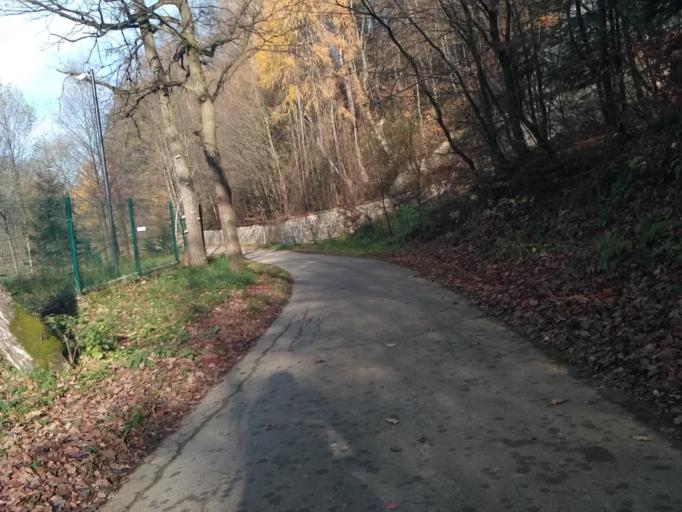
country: PL
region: Subcarpathian Voivodeship
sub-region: Powiat brzozowski
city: Turze Pole
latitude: 49.6836
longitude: 21.9971
